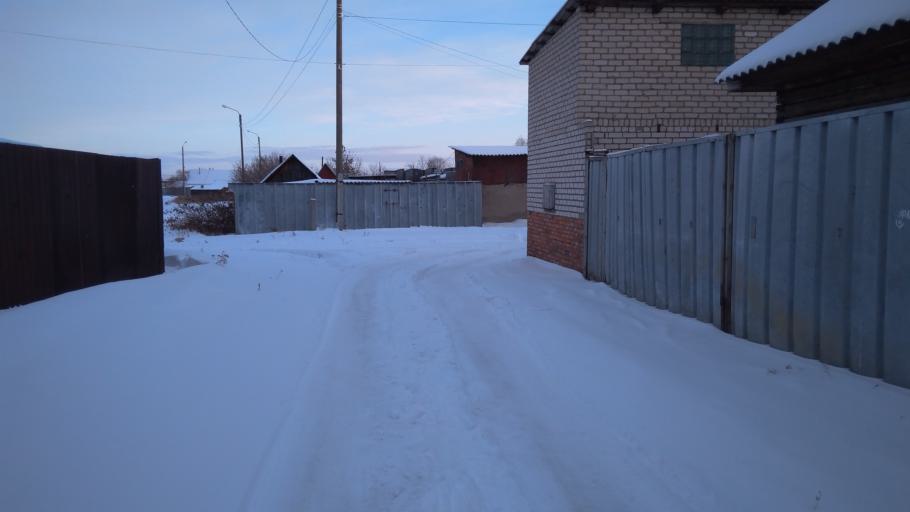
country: RU
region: Chelyabinsk
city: Troitsk
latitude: 54.0892
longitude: 61.5753
